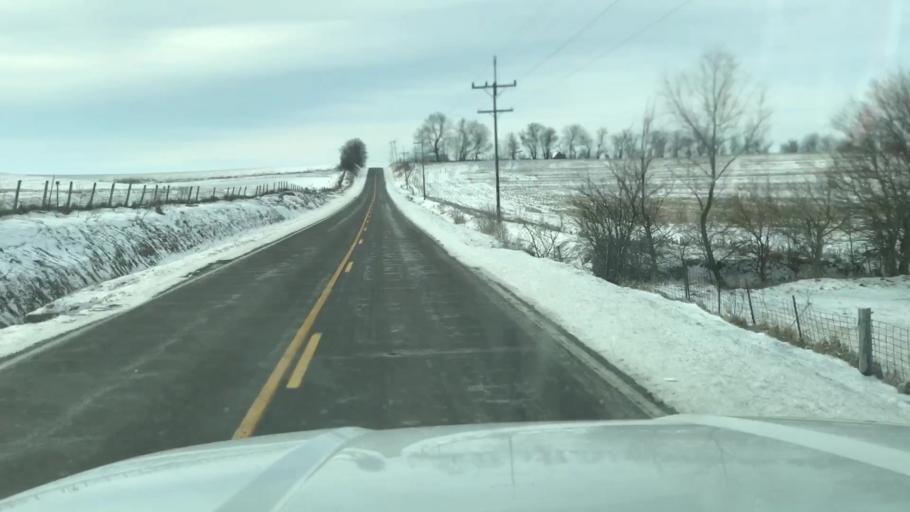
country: US
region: Missouri
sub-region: Holt County
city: Oregon
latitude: 40.0750
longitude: -95.1355
